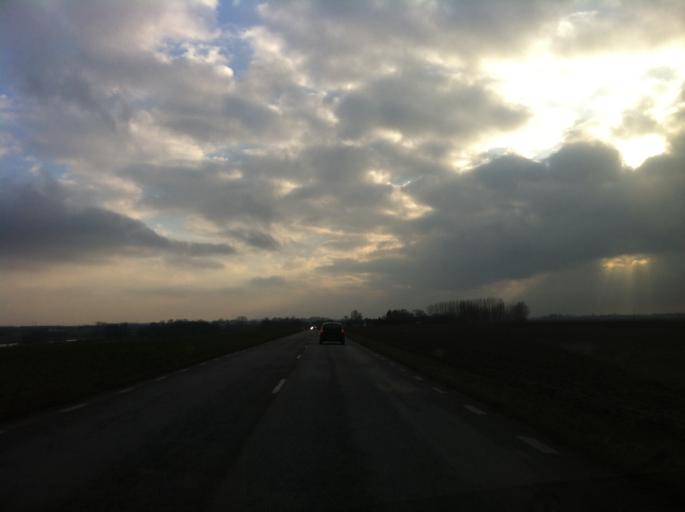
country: SE
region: Skane
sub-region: Kavlinge Kommun
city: Loddekopinge
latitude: 55.7754
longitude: 13.0608
